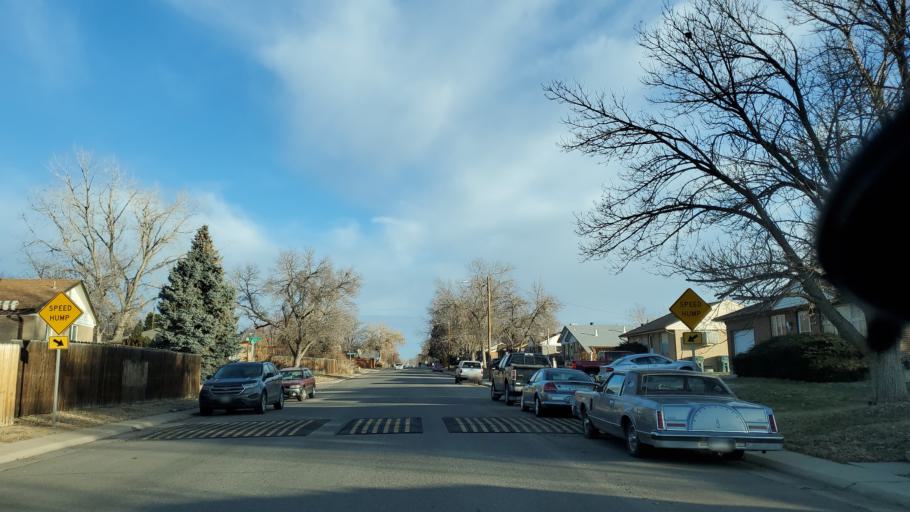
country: US
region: Colorado
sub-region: Adams County
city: Northglenn
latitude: 39.9017
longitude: -104.9613
